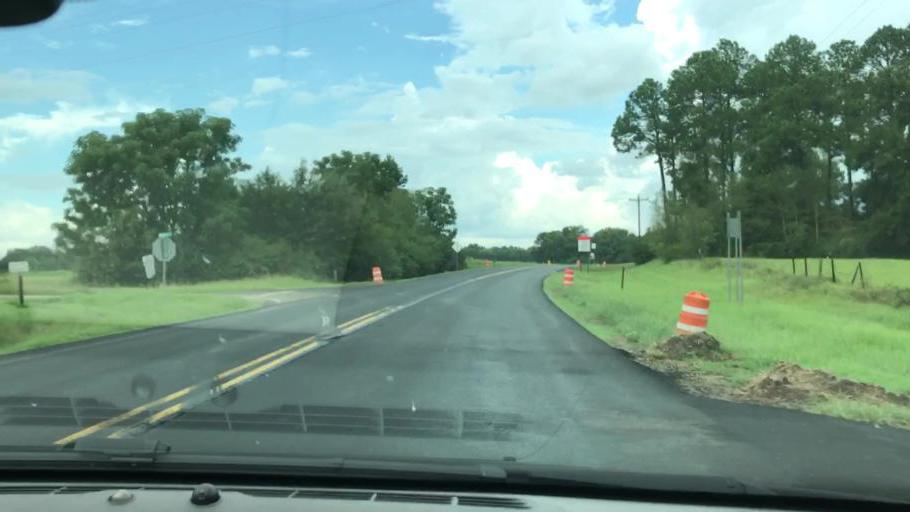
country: US
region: Georgia
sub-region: Early County
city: Blakely
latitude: 31.4019
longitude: -84.9595
